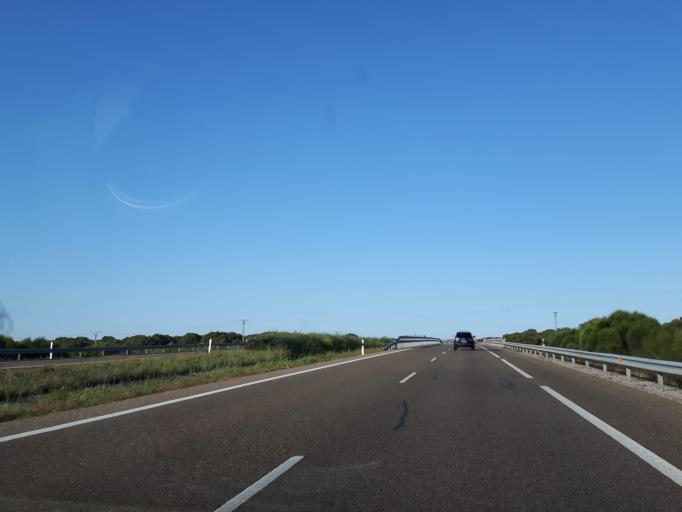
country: ES
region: Castille and Leon
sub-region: Provincia de Salamanca
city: Aldehuela de la Boveda
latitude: 40.8591
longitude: -6.0260
